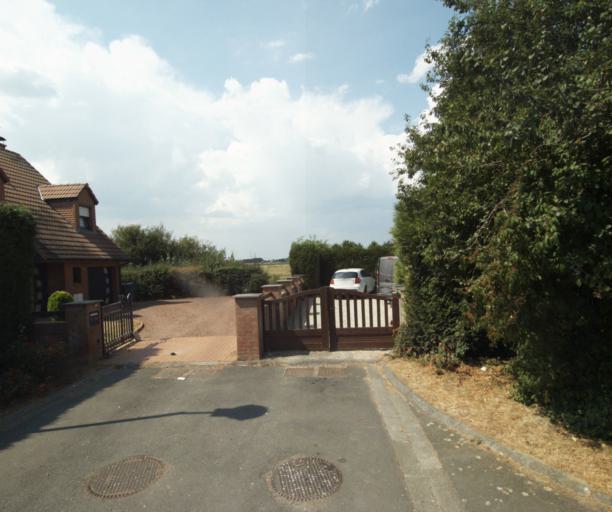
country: FR
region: Nord-Pas-de-Calais
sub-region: Departement du Nord
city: Deulemont
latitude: 50.7376
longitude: 2.9554
